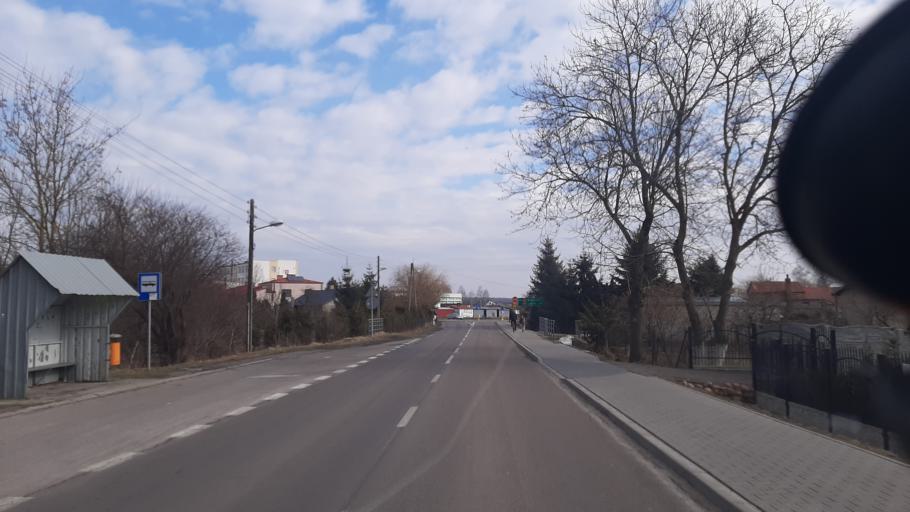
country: PL
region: Lublin Voivodeship
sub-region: Powiat lubelski
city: Niemce
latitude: 51.3585
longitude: 22.6205
